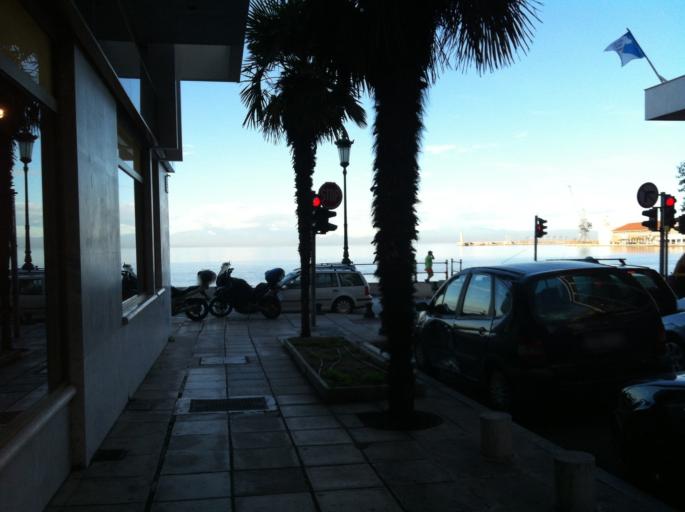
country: GR
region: Central Macedonia
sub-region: Nomos Thessalonikis
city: Thessaloniki
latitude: 40.6330
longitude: 22.9393
